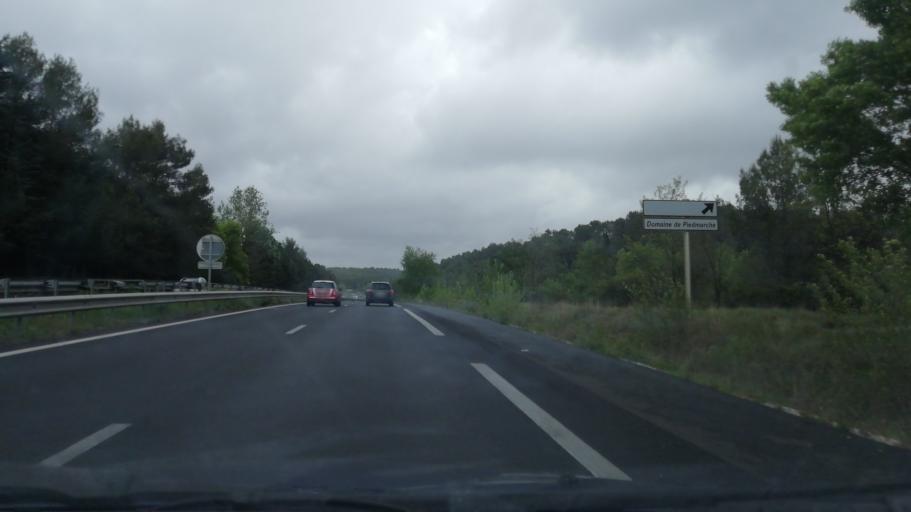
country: FR
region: Languedoc-Roussillon
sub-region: Departement de l'Herault
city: Saint-Clement-de-Riviere
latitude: 43.6646
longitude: 3.8292
